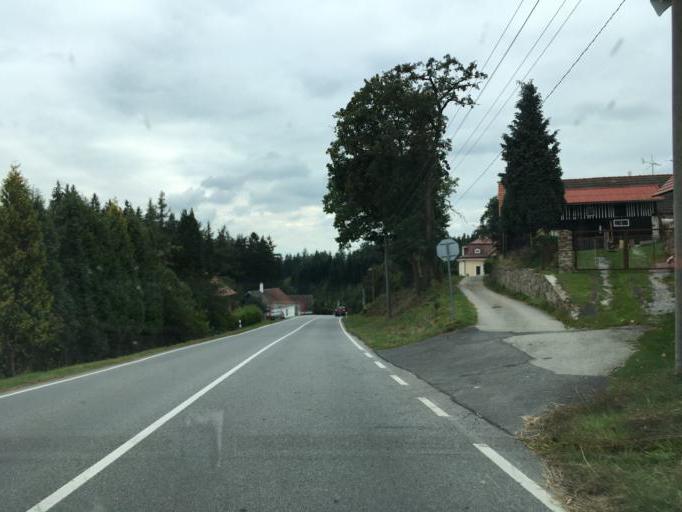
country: CZ
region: Vysocina
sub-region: Okres Pelhrimov
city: Zeliv
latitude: 49.5339
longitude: 15.1682
